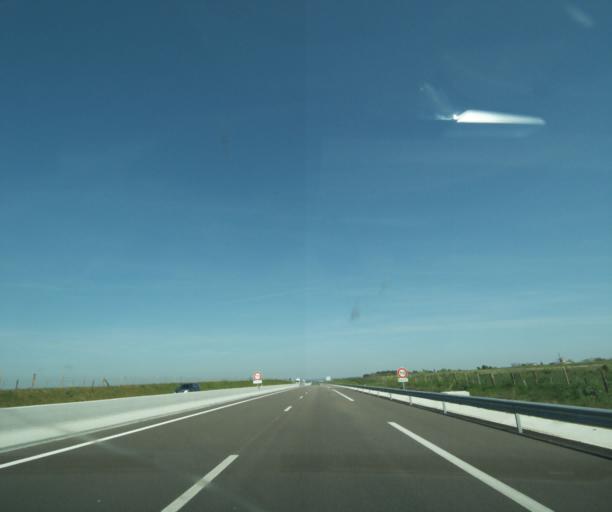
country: FR
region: Bourgogne
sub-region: Departement de la Nievre
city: Saint-Pierre-le-Moutier
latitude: 46.8059
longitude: 3.1209
